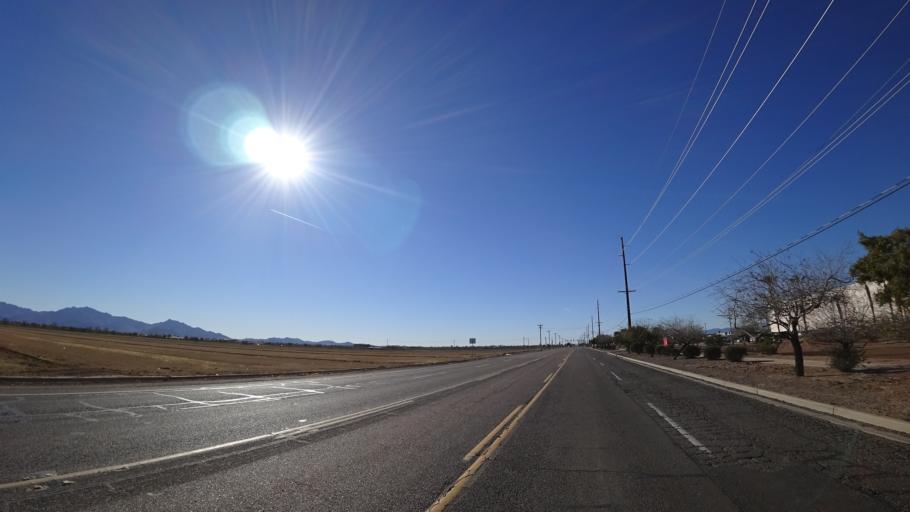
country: US
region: Arizona
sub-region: Maricopa County
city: Tolleson
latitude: 33.4357
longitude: -112.2684
